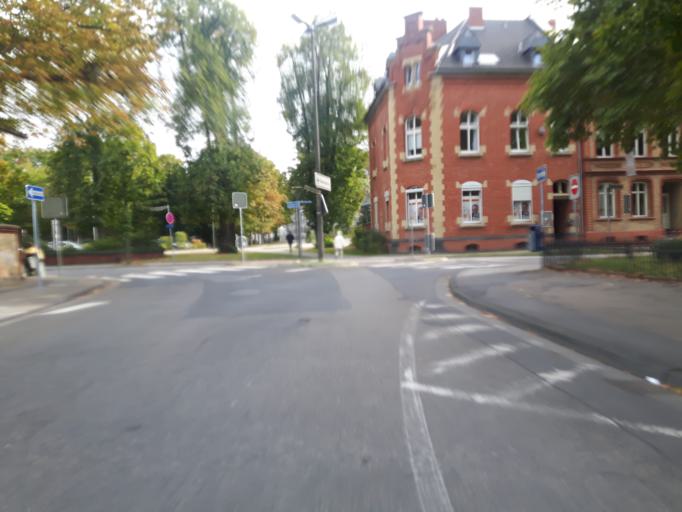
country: DE
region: Rheinland-Pfalz
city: Neuwied
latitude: 50.4307
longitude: 7.4644
